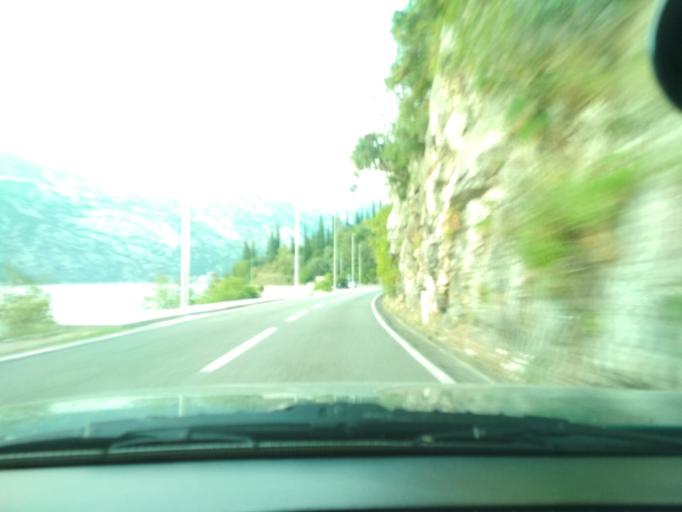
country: ME
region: Kotor
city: Risan
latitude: 42.4991
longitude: 18.6923
